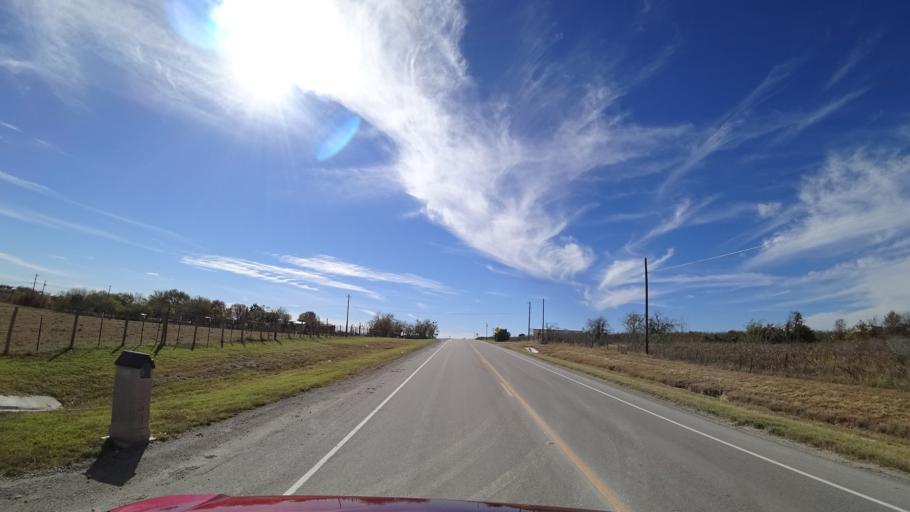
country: US
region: Texas
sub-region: Travis County
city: Onion Creek
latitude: 30.1203
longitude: -97.6902
